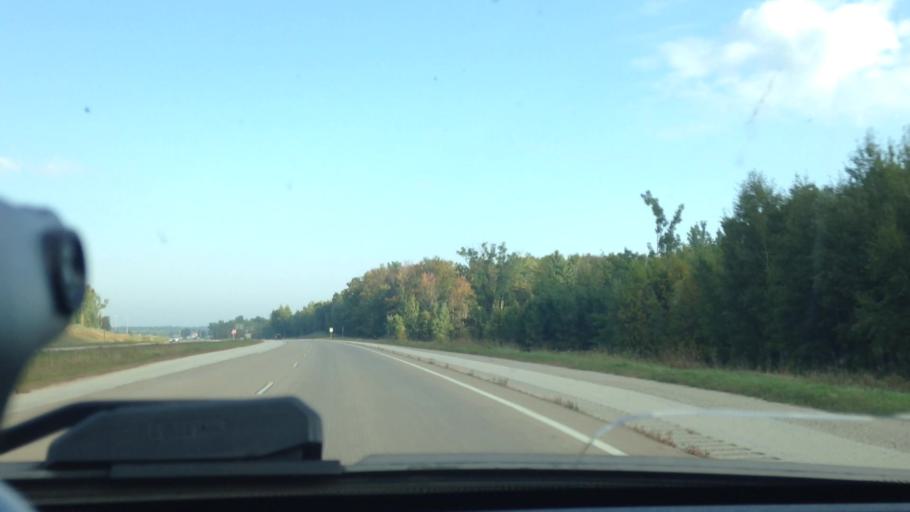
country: US
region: Wisconsin
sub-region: Oconto County
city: Oconto Falls
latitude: 44.9705
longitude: -88.0368
